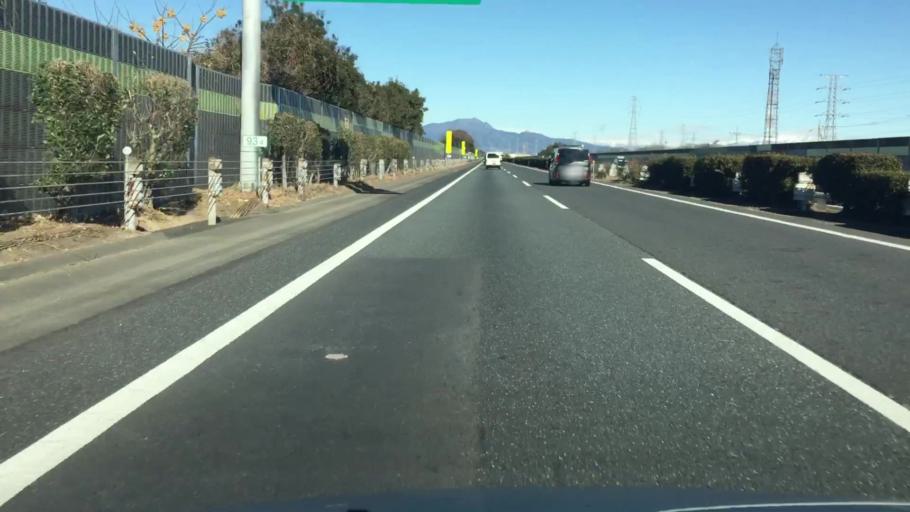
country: JP
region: Gunma
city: Maebashi-shi
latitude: 36.3857
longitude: 139.0263
